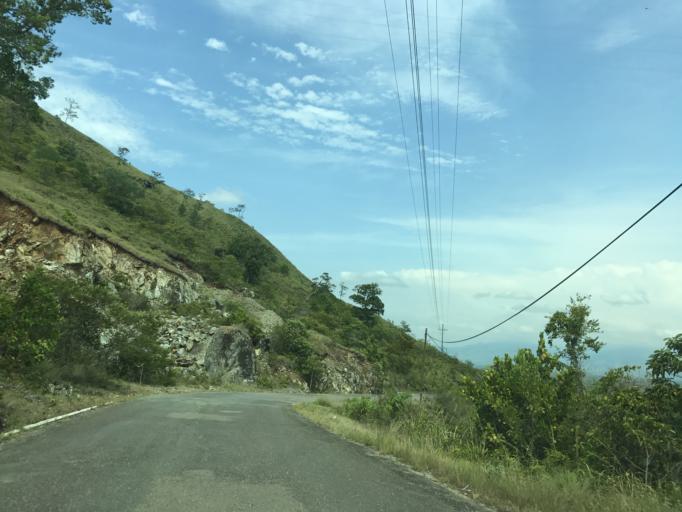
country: GT
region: Izabal
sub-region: Municipio de Los Amates
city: Los Amates
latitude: 15.3881
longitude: -89.0279
